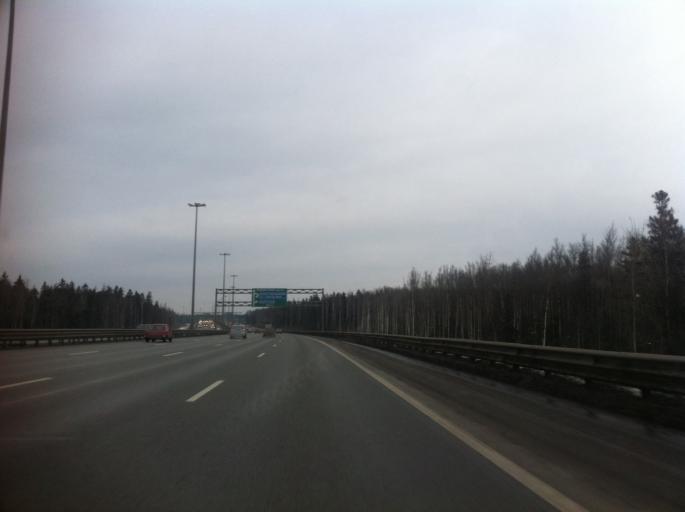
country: RU
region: Leningrad
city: Rybatskoye
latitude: 59.9122
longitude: 30.5261
